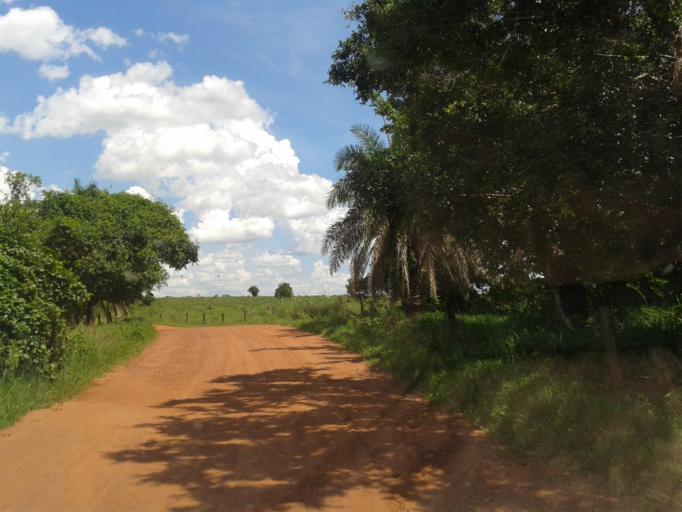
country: BR
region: Minas Gerais
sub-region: Santa Vitoria
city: Santa Vitoria
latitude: -19.1476
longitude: -50.6181
